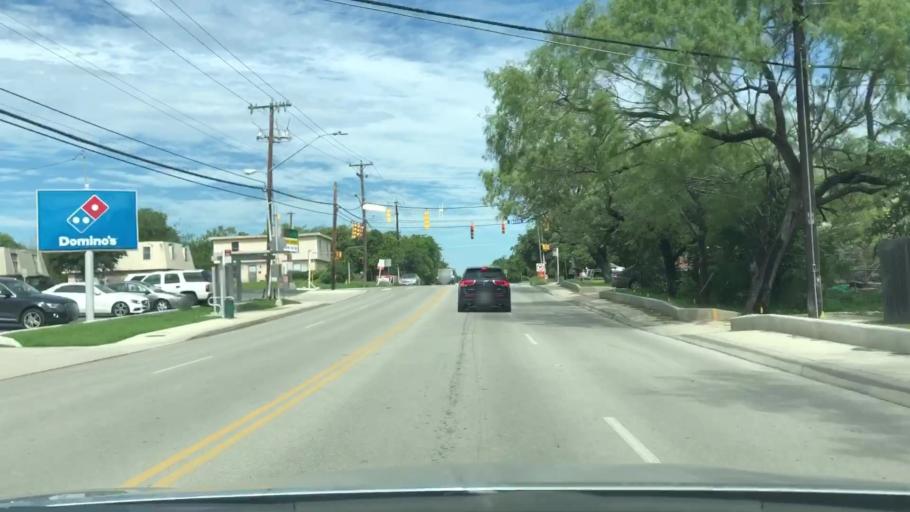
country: US
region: Texas
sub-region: Bexar County
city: Olmos Park
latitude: 29.5037
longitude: -98.4917
